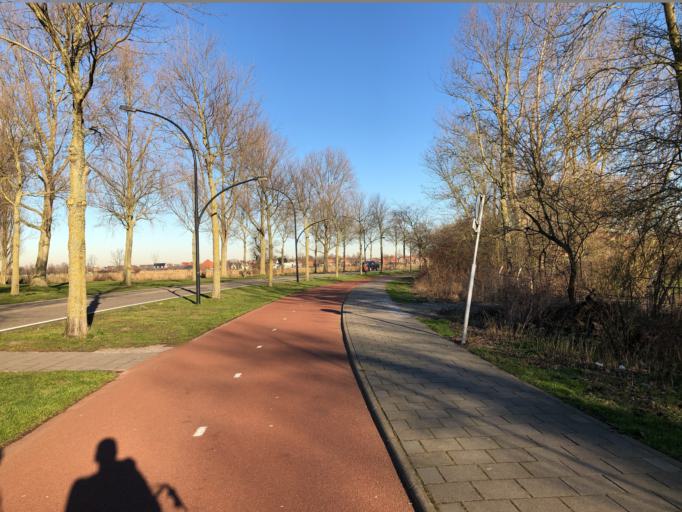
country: NL
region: North Holland
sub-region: Gemeente Uitgeest
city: Uitgeest
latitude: 52.5071
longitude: 4.7633
